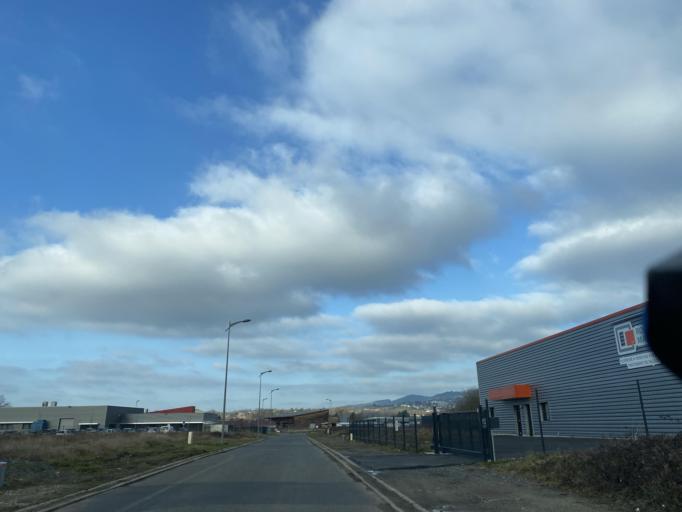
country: FR
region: Auvergne
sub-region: Departement du Puy-de-Dome
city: Peschadoires
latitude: 45.8367
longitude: 3.5139
